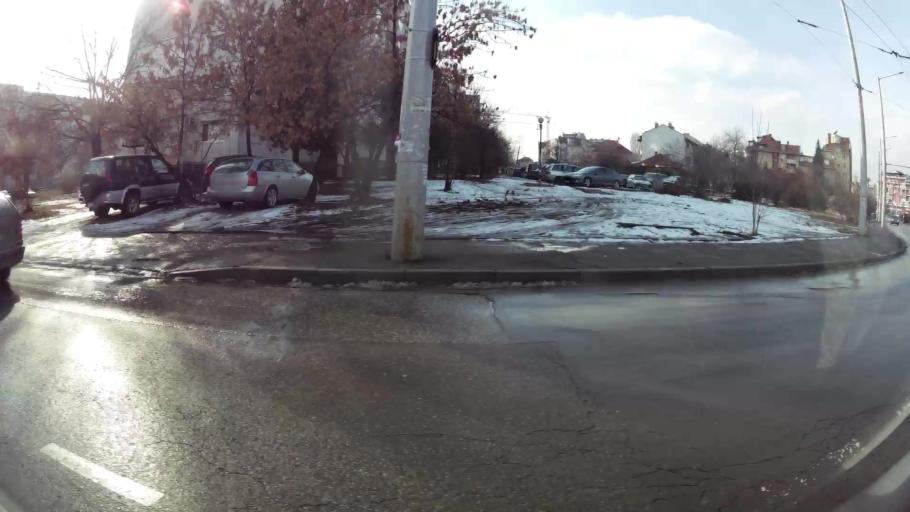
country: BG
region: Sofiya
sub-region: Obshtina Bozhurishte
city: Bozhurishte
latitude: 42.7231
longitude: 23.2609
